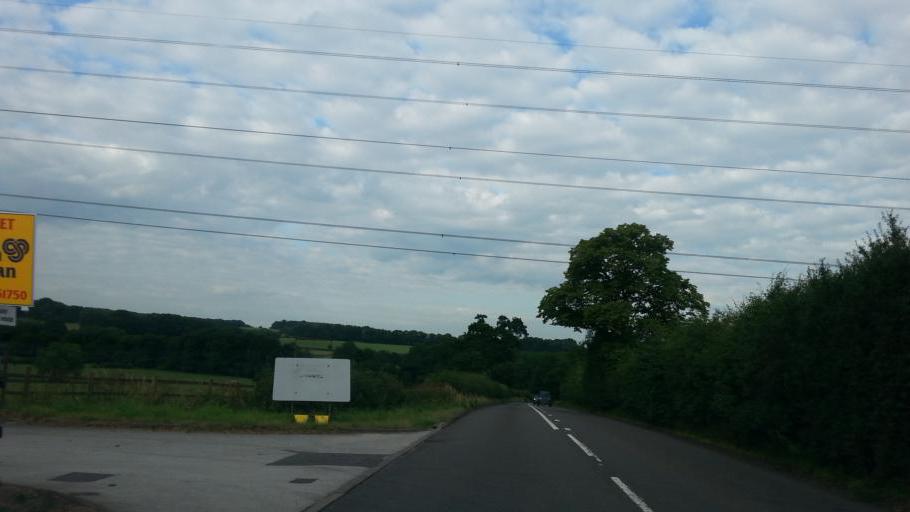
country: GB
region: England
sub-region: Staffordshire
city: Uttoxeter
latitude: 52.8872
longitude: -1.8928
